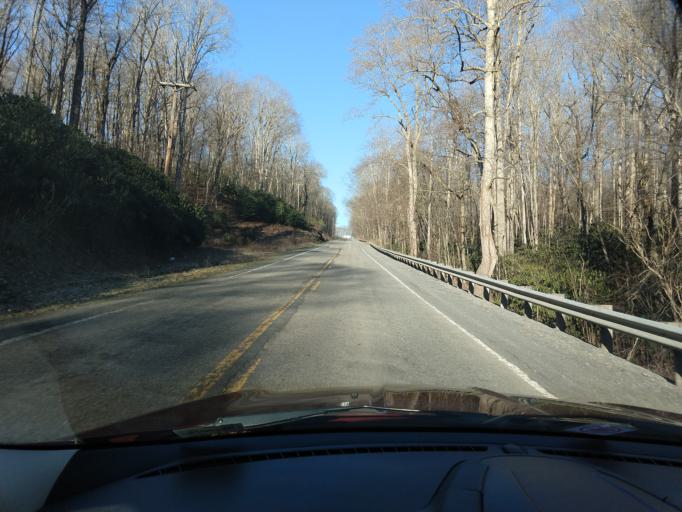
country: US
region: West Virginia
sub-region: Fayette County
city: Fayetteville
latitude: 38.0493
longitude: -80.9454
